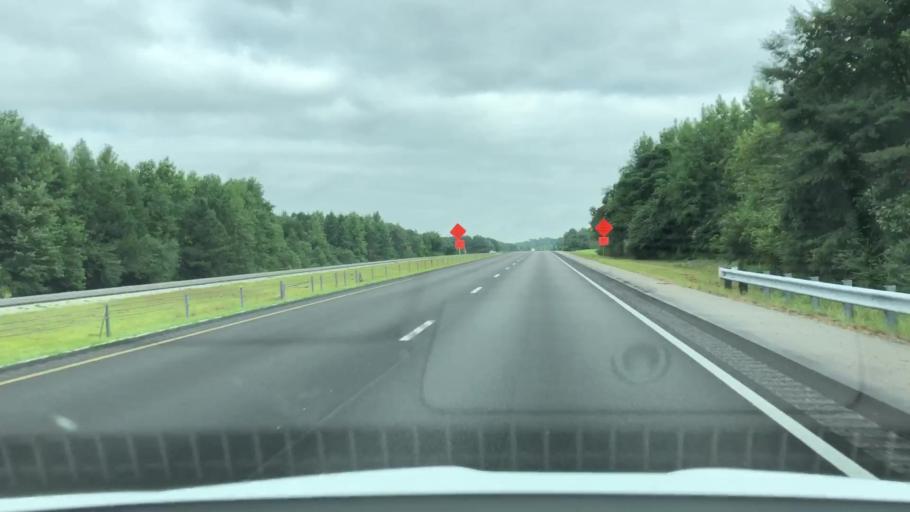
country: US
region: North Carolina
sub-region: Wayne County
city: Fremont
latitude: 35.5724
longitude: -77.9888
